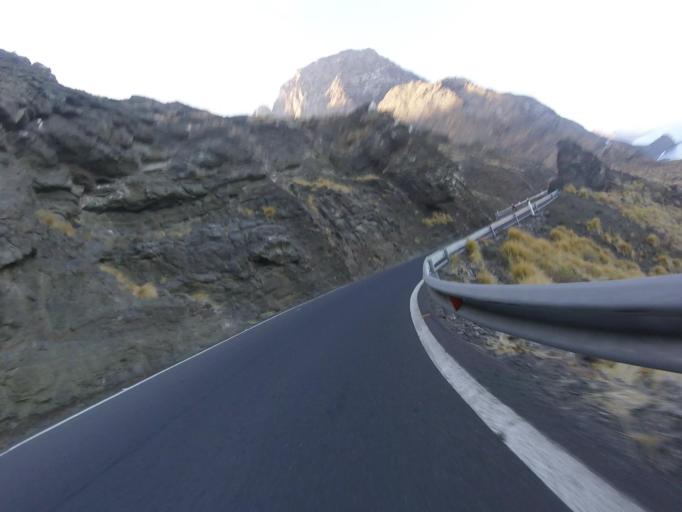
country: ES
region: Canary Islands
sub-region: Provincia de Las Palmas
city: Agaete
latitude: 28.0729
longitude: -15.7157
